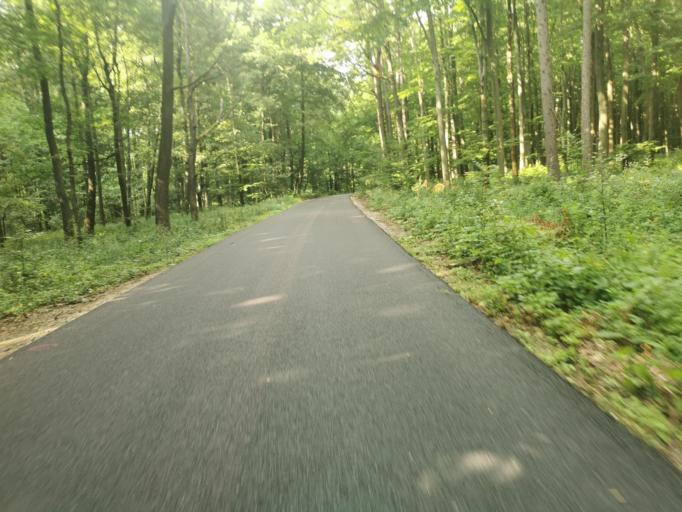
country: SK
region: Trenciansky
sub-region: Okres Myjava
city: Myjava
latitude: 48.8087
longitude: 17.6016
